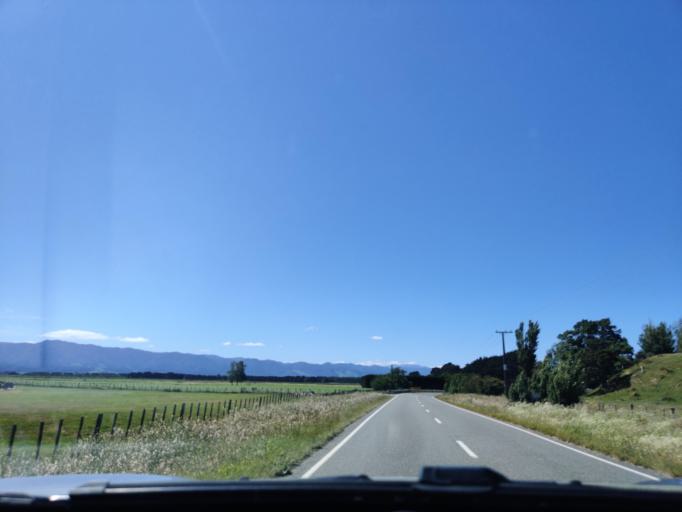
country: NZ
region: Wellington
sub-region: Upper Hutt City
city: Upper Hutt
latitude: -41.3303
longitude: 175.2112
